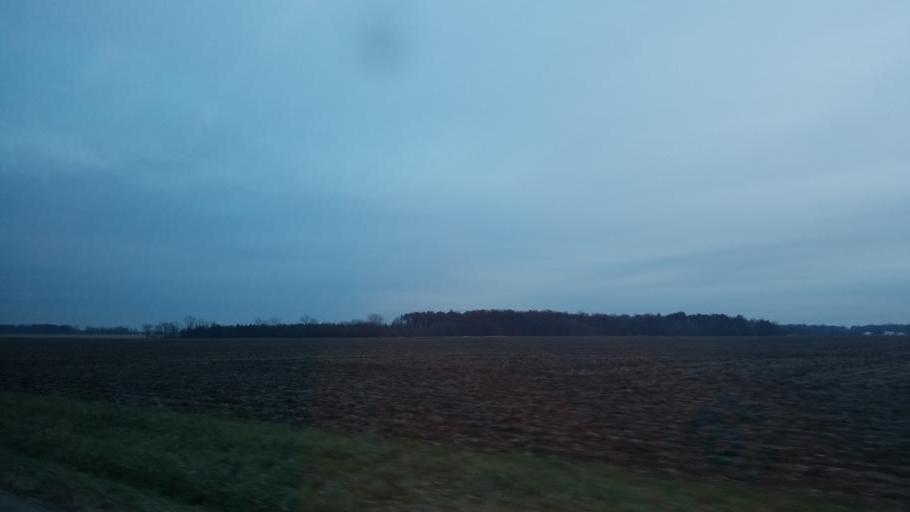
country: US
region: Indiana
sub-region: Adams County
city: Decatur
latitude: 40.7874
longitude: -85.0123
